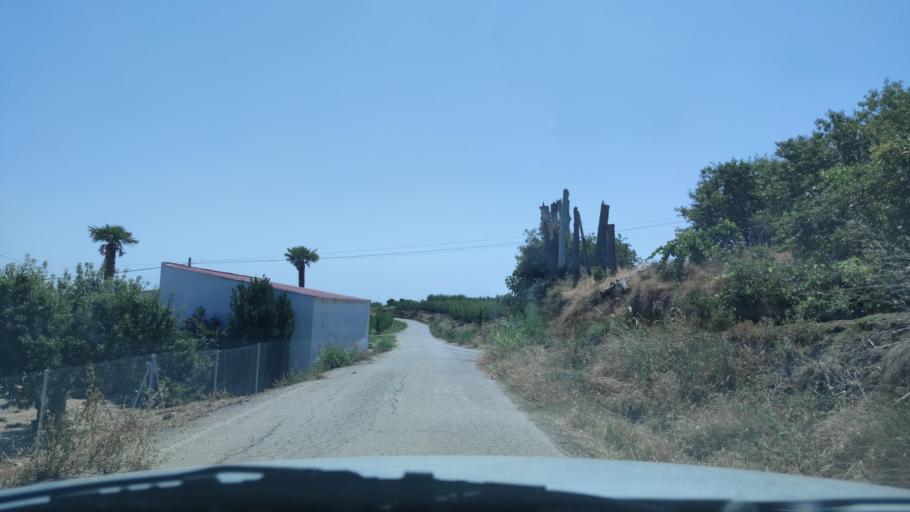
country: ES
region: Catalonia
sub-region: Provincia de Lleida
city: Torrefarrera
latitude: 41.6439
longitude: 0.5905
